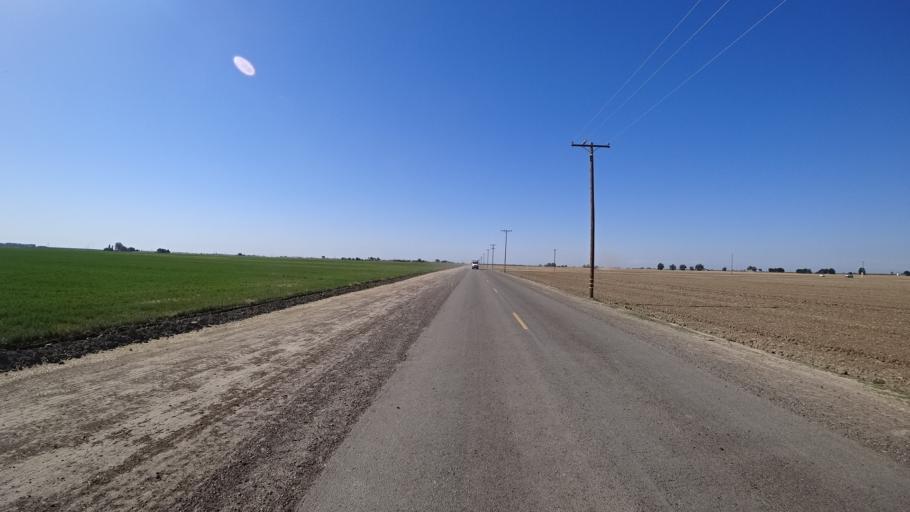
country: US
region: California
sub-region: Kings County
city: Home Garden
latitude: 36.2349
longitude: -119.5562
